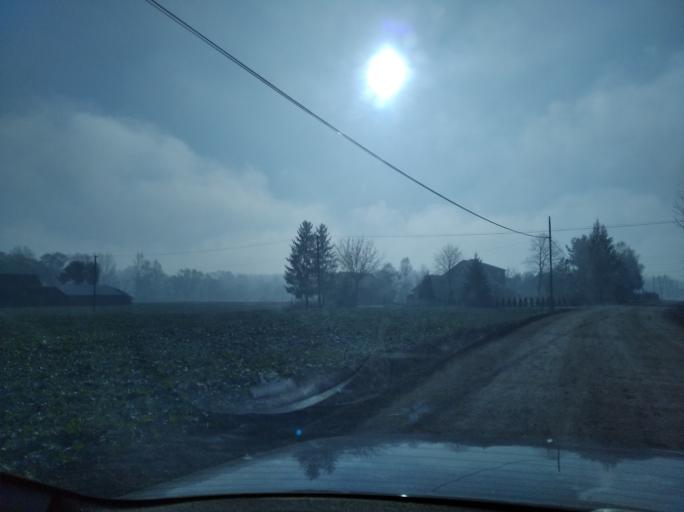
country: PL
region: Subcarpathian Voivodeship
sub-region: Powiat strzyzowski
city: Wisniowa
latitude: 49.8709
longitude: 21.7061
